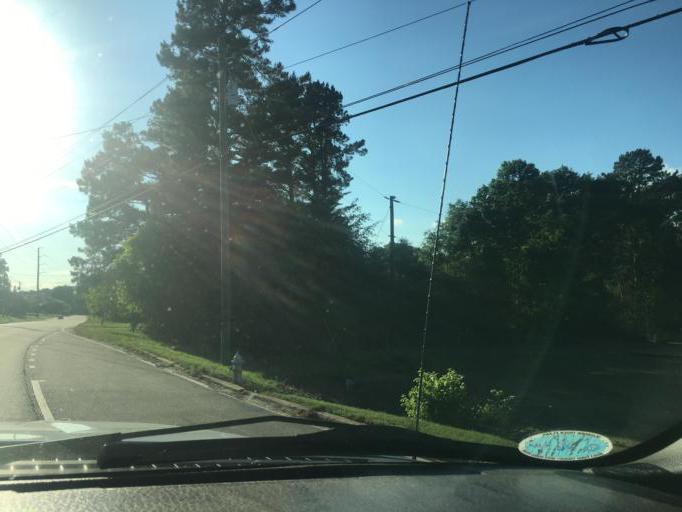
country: US
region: Georgia
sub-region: Forsyth County
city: Cumming
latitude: 34.2730
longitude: -84.1071
